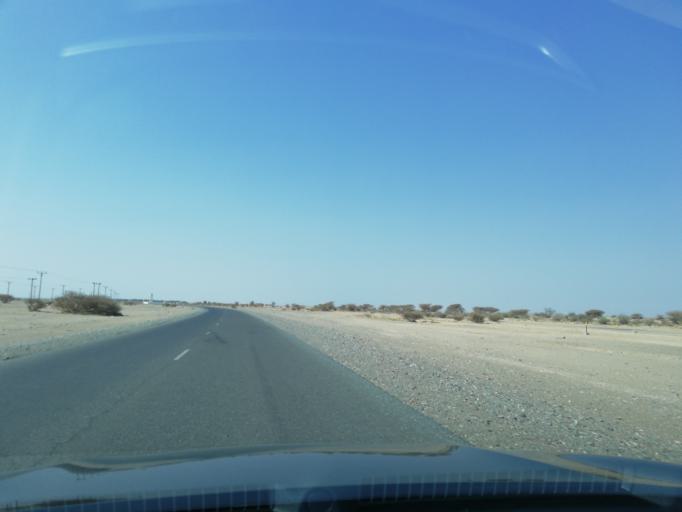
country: OM
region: Muhafazat ad Dakhiliyah
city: Adam
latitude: 22.3226
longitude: 58.0662
